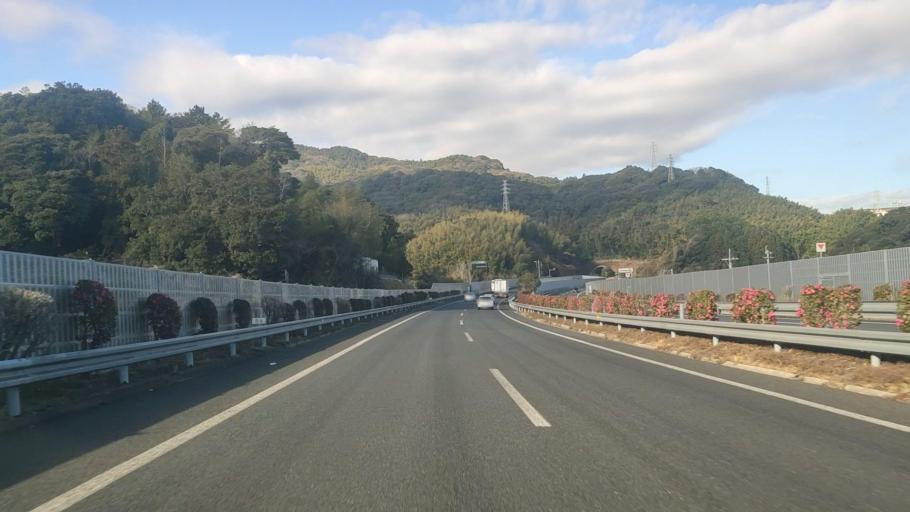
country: JP
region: Fukuoka
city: Kanda
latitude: 33.7995
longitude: 130.9547
